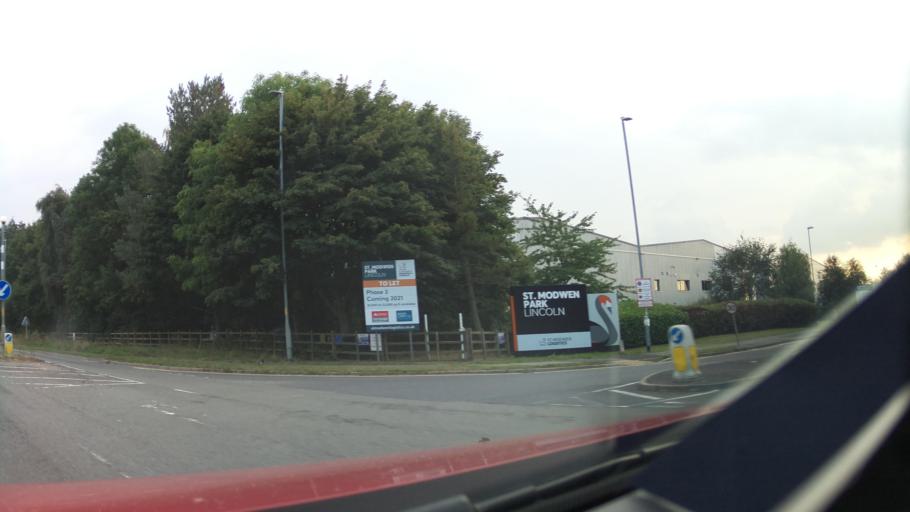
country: GB
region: England
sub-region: Nottinghamshire
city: South Collingham
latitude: 53.1504
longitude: -0.6700
